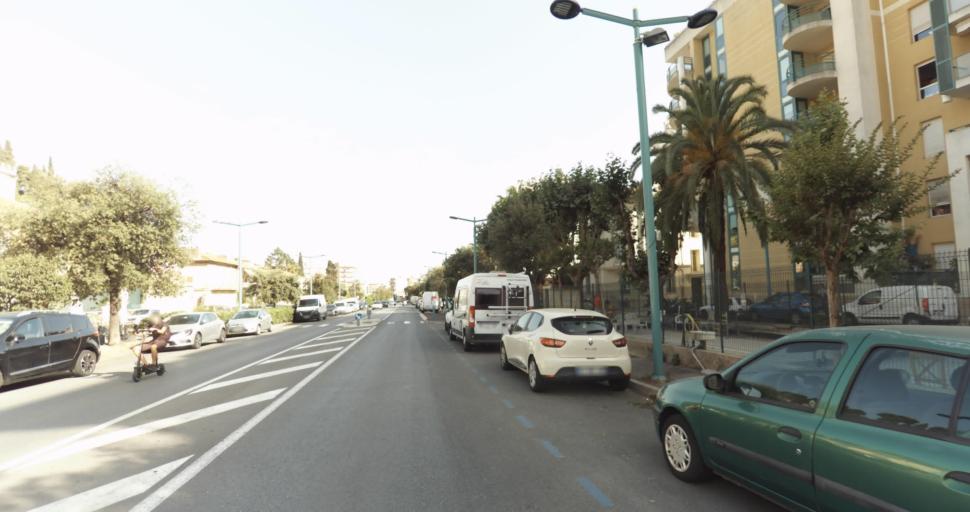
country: FR
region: Provence-Alpes-Cote d'Azur
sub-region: Departement des Alpes-Maritimes
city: Roquebrune-Cap-Martin
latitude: 43.7752
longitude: 7.4889
